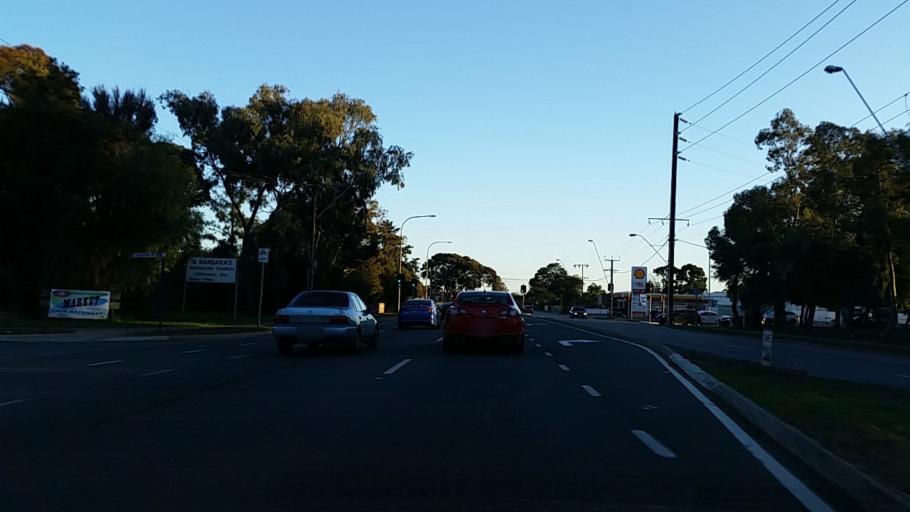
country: AU
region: South Australia
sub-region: Salisbury
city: Salisbury
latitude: -34.7874
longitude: 138.6191
